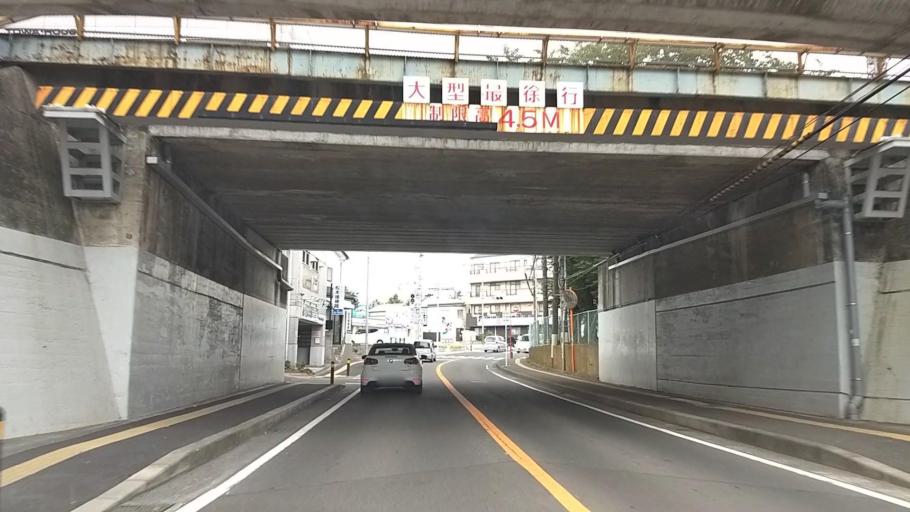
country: JP
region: Kanagawa
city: Isehara
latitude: 35.3967
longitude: 139.3152
